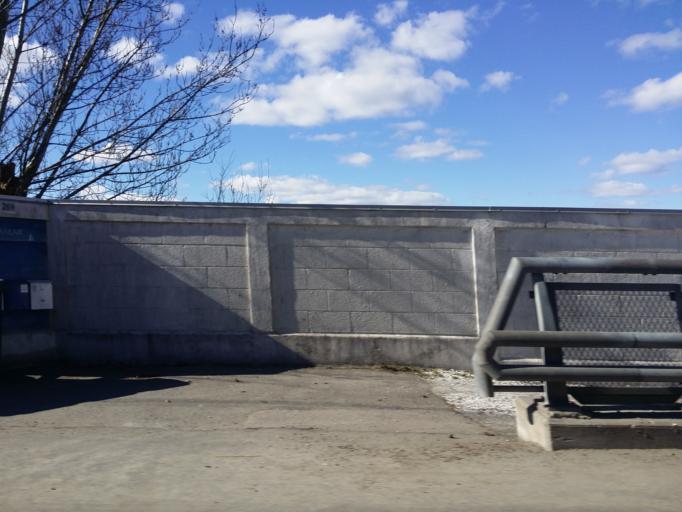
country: NO
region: Akershus
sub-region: Oppegard
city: Kolbotn
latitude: 59.8479
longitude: 10.7783
